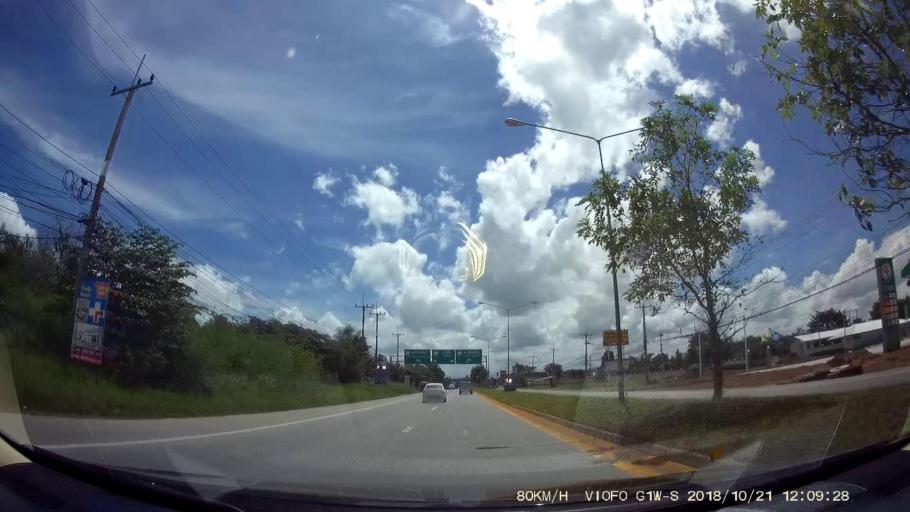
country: TH
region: Chaiyaphum
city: Chatturat
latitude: 15.4209
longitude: 101.8326
